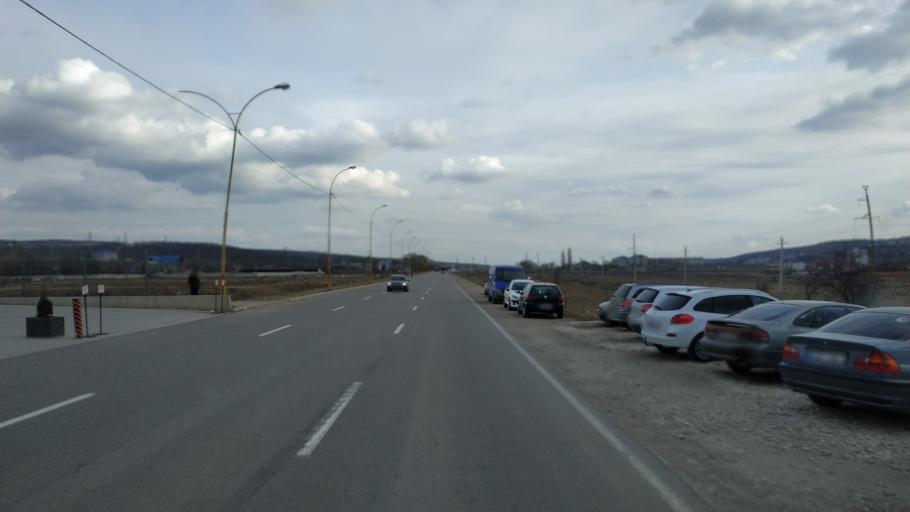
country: MD
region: Hincesti
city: Hincesti
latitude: 46.8297
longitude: 28.6002
